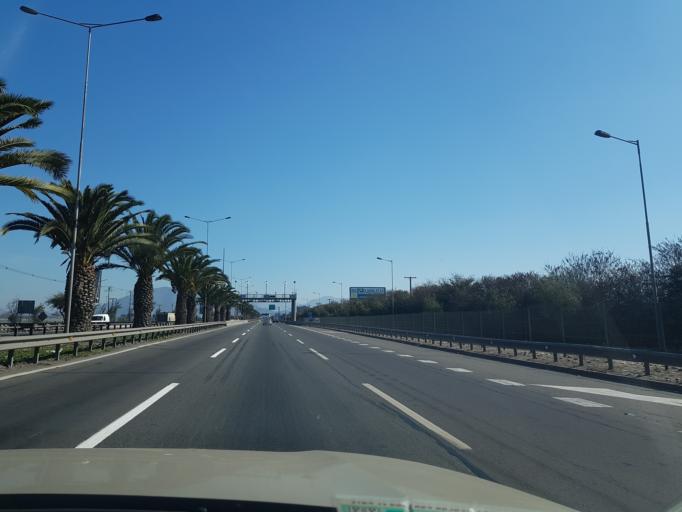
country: CL
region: Santiago Metropolitan
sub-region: Provincia de Santiago
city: Lo Prado
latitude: -33.3984
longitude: -70.7743
